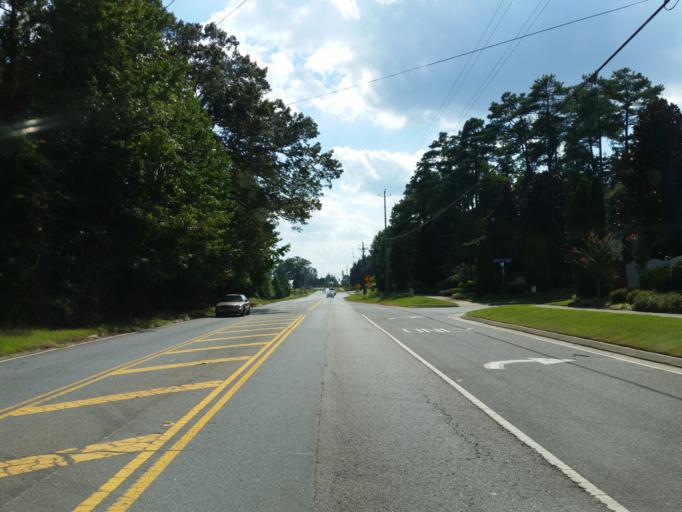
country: US
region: Georgia
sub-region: Gwinnett County
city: Lawrenceville
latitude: 33.9658
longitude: -83.9645
